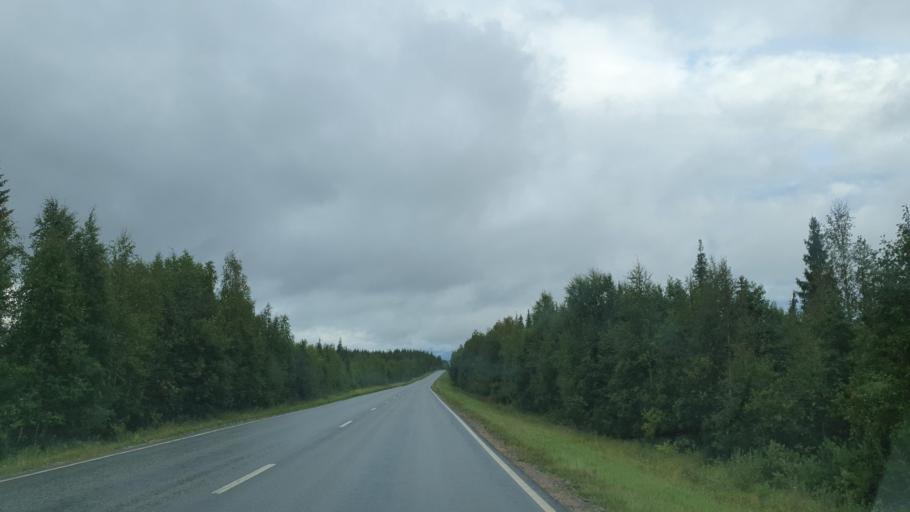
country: FI
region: Lapland
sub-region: Tunturi-Lappi
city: Kolari
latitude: 67.3962
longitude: 23.8055
